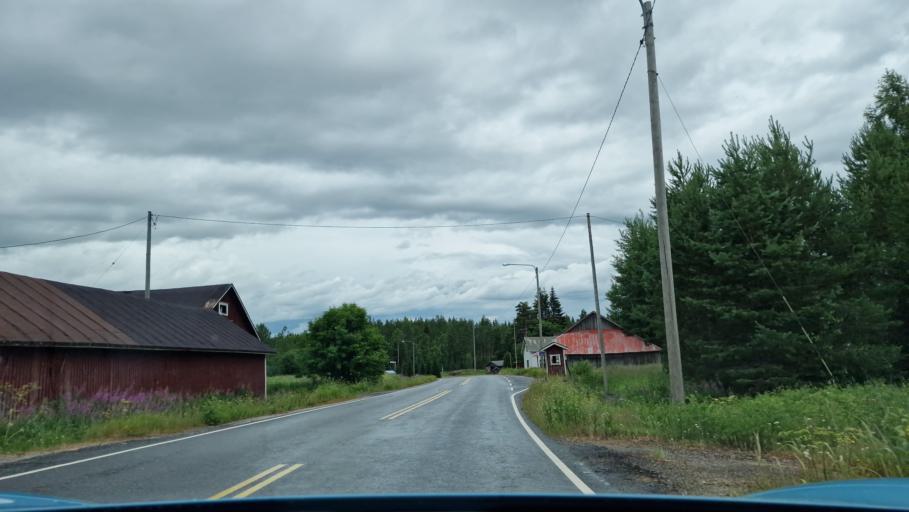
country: FI
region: Southern Ostrobothnia
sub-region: Jaerviseutu
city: Soini
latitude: 62.7009
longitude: 24.4531
